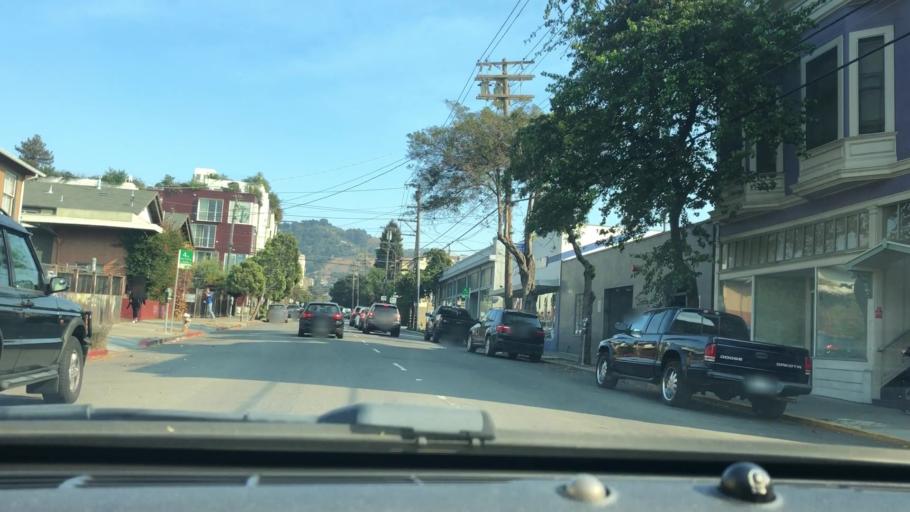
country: US
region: California
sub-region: Alameda County
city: Berkeley
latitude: 37.8641
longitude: -122.2662
